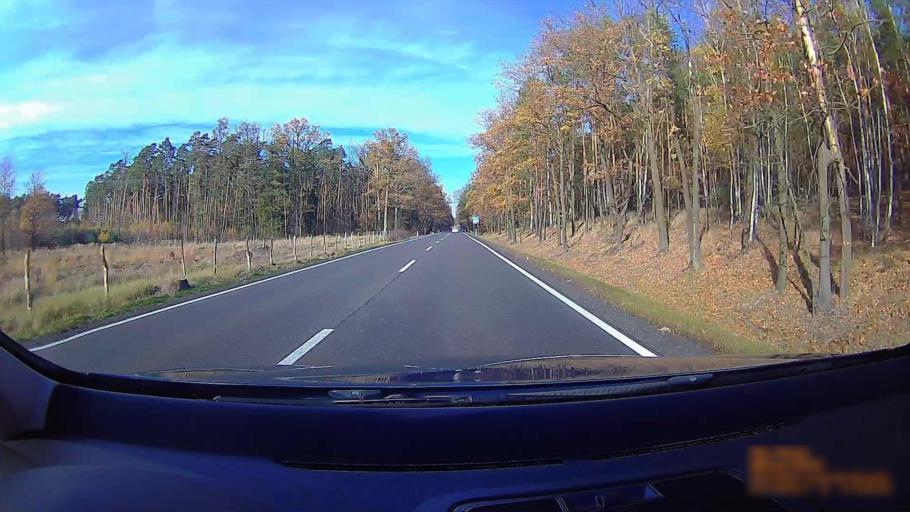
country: PL
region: Greater Poland Voivodeship
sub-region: Powiat ostrowski
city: Przygodzice
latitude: 51.5031
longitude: 17.8500
